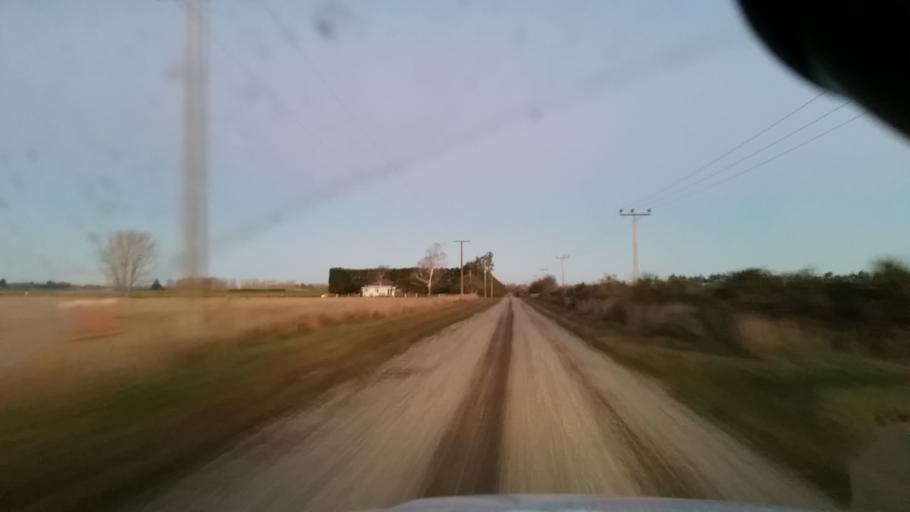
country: NZ
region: Canterbury
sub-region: Ashburton District
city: Tinwald
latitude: -43.9961
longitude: 171.6624
